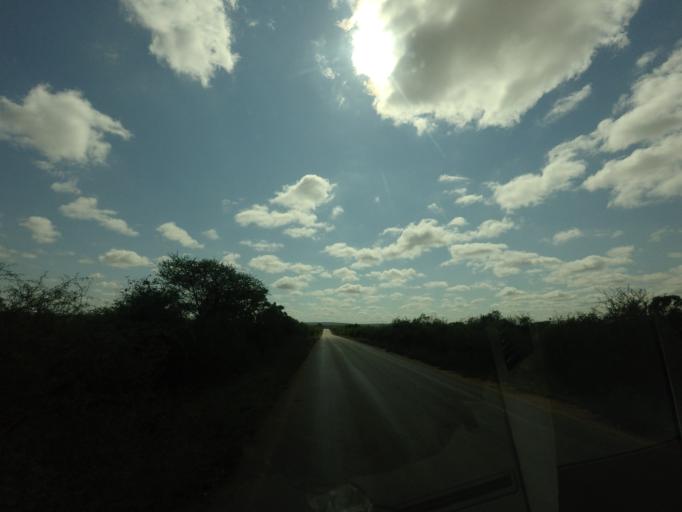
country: ZA
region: Mpumalanga
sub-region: Ehlanzeni District
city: Komatipoort
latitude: -25.1248
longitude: 31.9197
